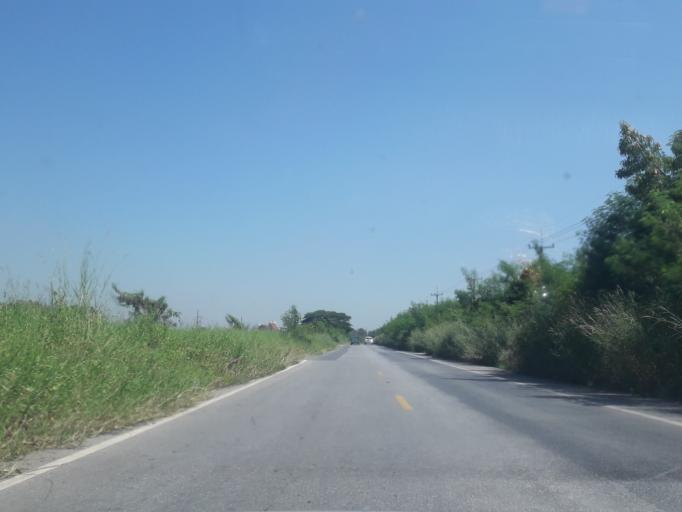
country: TH
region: Sara Buri
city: Nong Khae
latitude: 14.2970
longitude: 100.8387
